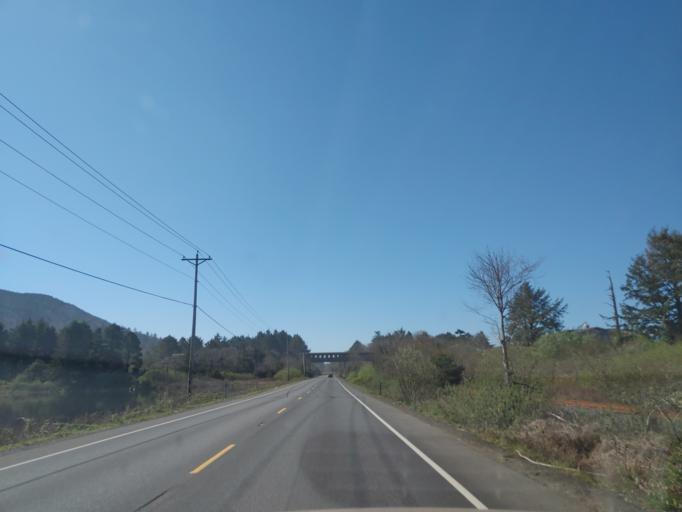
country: US
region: Oregon
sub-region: Tillamook County
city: Rockaway Beach
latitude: 45.5945
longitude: -123.9474
